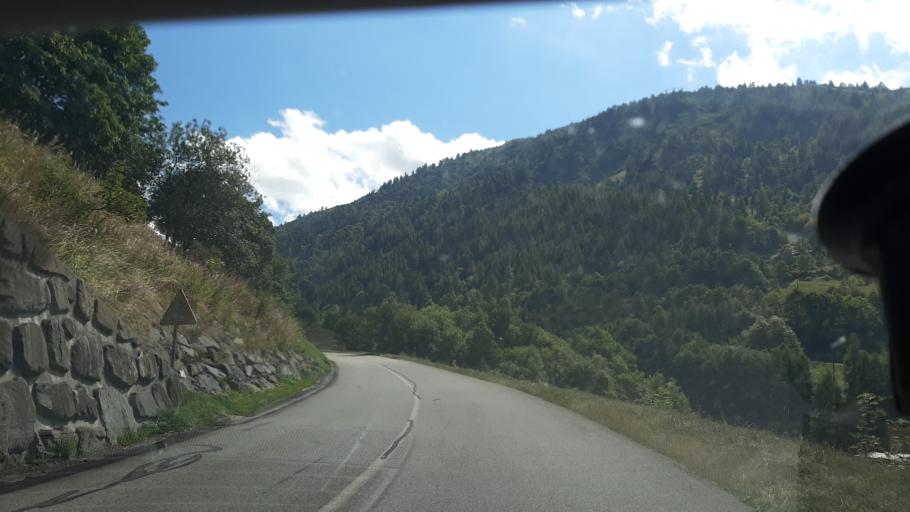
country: FR
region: Rhone-Alpes
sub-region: Departement de la Savoie
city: Saint-Michel-de-Maurienne
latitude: 45.1825
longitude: 6.4808
